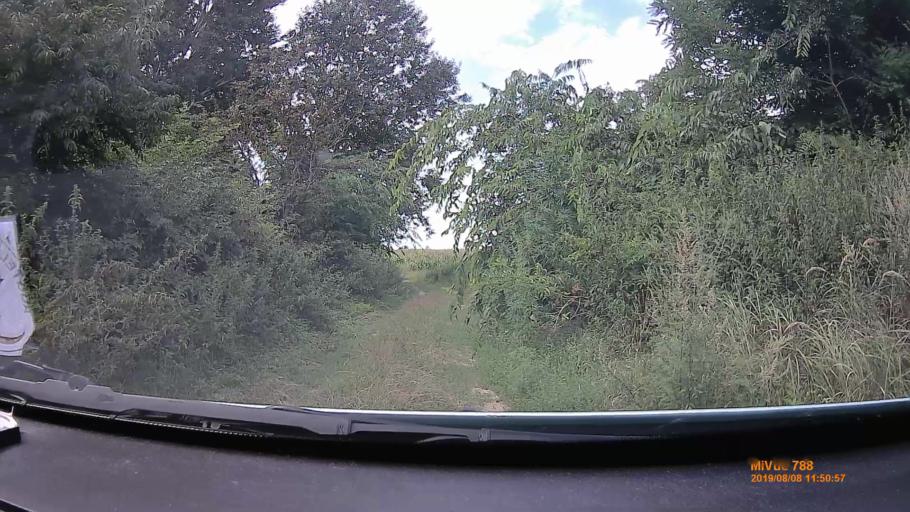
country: HU
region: Szabolcs-Szatmar-Bereg
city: Nyirmihalydi
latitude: 47.7252
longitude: 21.9472
